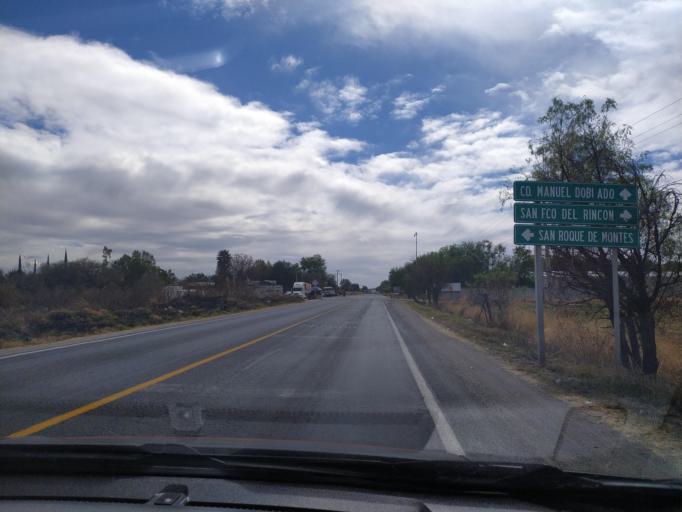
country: LA
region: Oudomxai
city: Muang La
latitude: 21.0220
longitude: 101.8262
